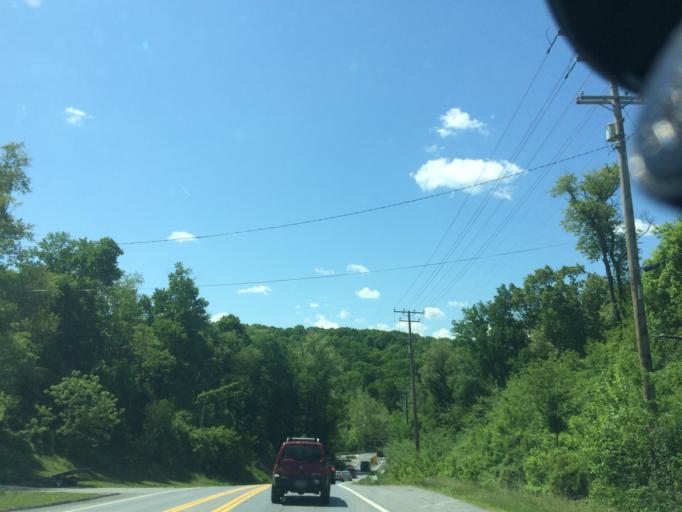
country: US
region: Maryland
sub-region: Carroll County
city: Sykesville
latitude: 39.3546
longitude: -77.0159
